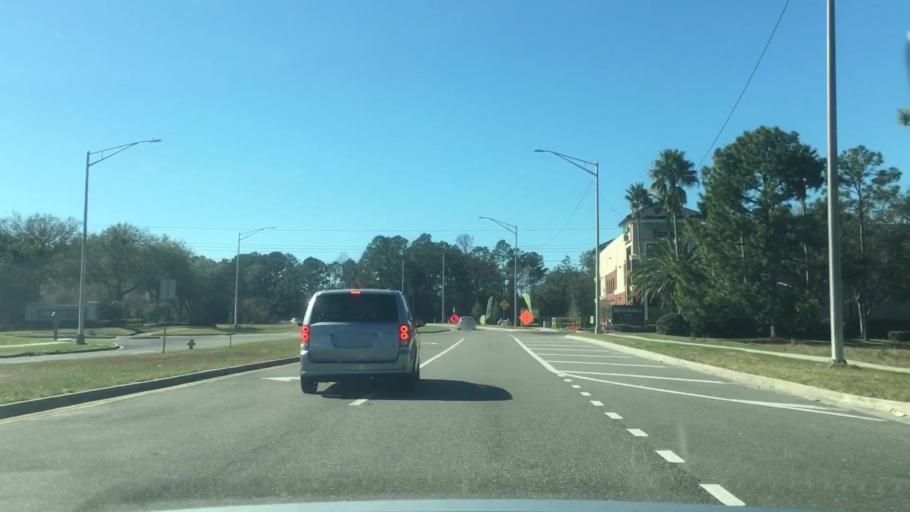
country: US
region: Florida
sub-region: Duval County
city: Jacksonville
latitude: 30.2477
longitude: -81.5402
